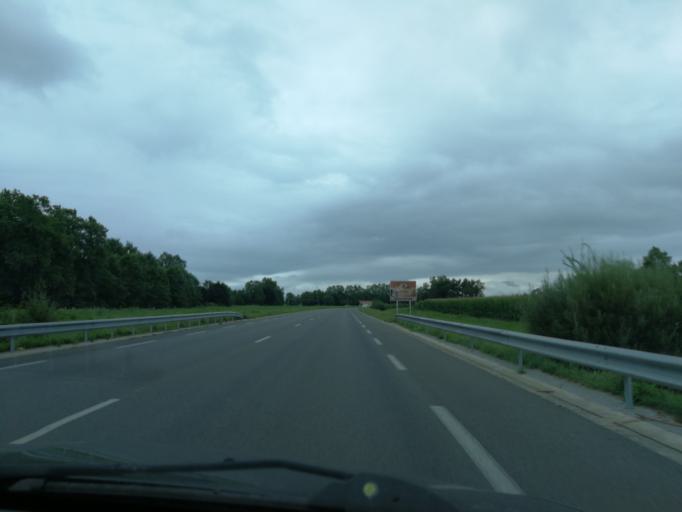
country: FR
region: Midi-Pyrenees
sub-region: Departement des Hautes-Pyrenees
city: Bazet
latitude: 43.2605
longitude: 0.0663
